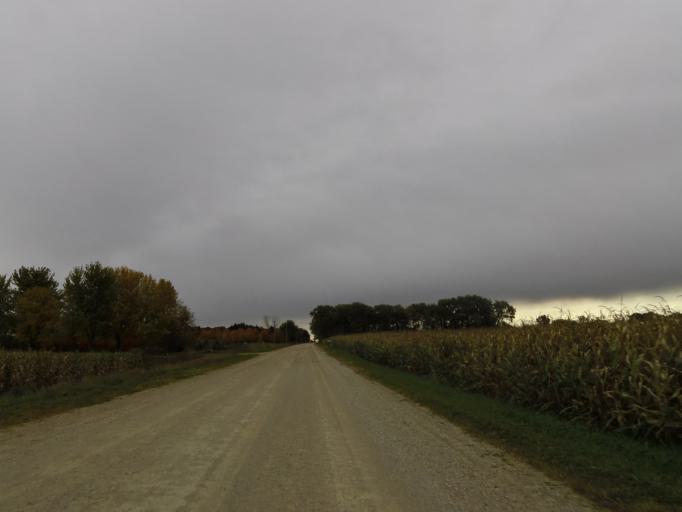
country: US
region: Minnesota
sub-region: Scott County
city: Prior Lake
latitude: 44.7034
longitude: -93.5128
